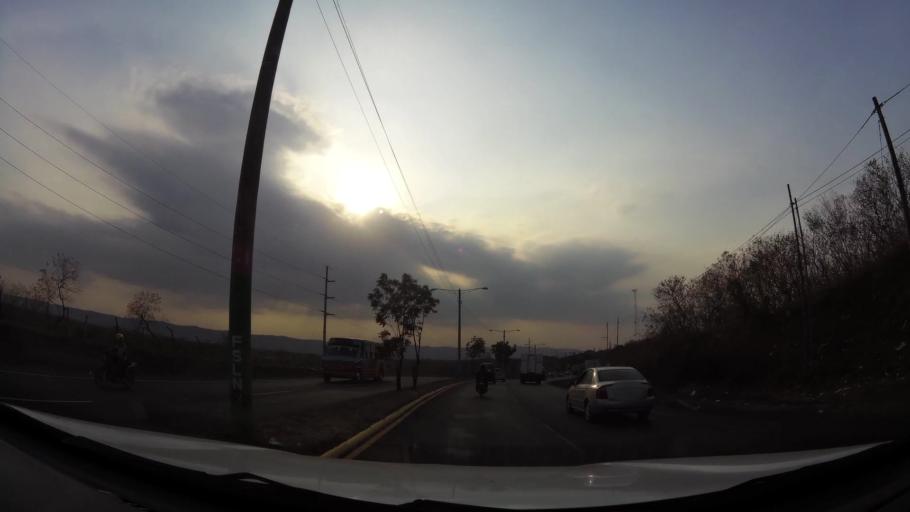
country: NI
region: Managua
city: Ciudad Sandino
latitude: 12.1347
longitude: -86.3256
